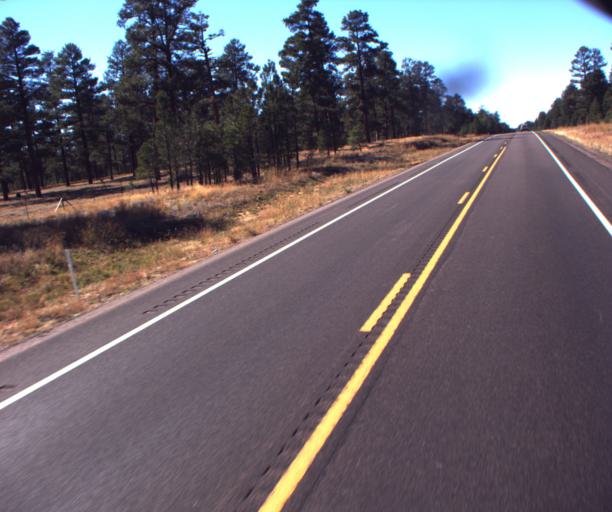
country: US
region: Arizona
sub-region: Apache County
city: Saint Michaels
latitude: 35.6934
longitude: -109.2656
